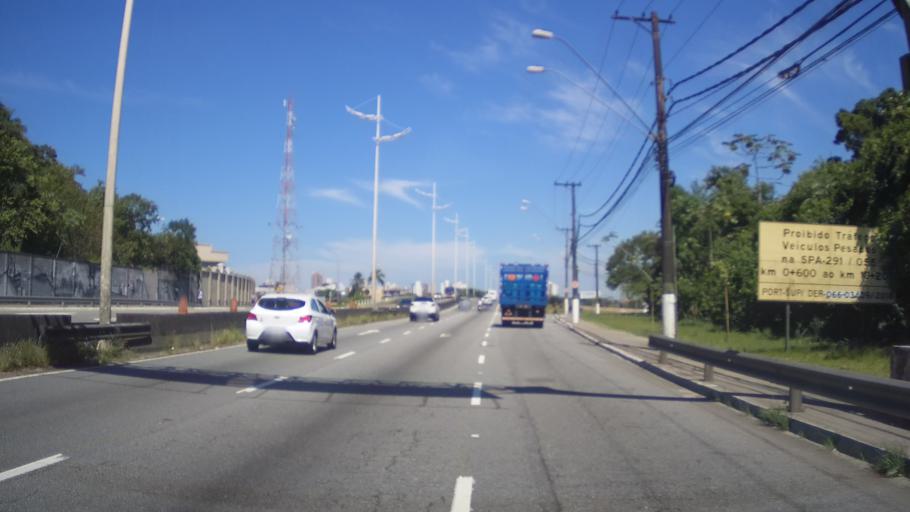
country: BR
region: Sao Paulo
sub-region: Praia Grande
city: Praia Grande
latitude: -23.9976
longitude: -46.4108
